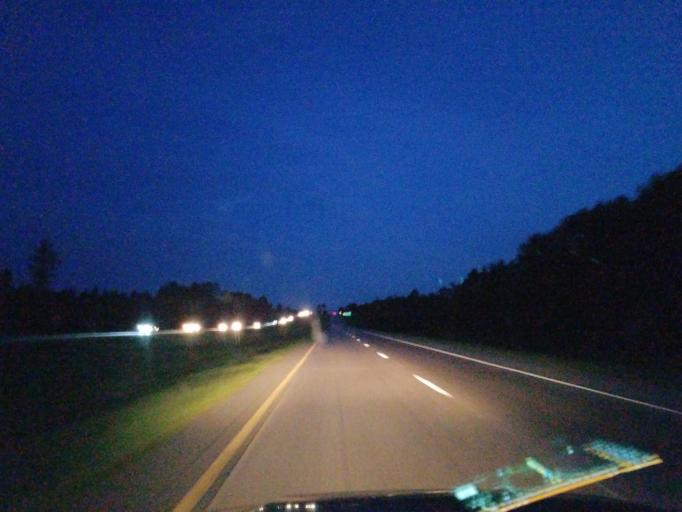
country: US
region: Mississippi
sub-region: Forrest County
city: Rawls Springs
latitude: 31.4792
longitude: -89.3239
